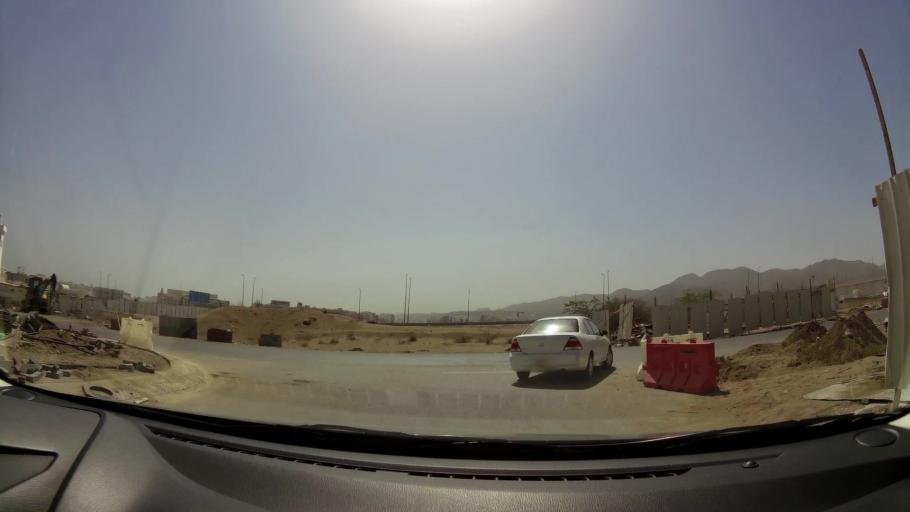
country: OM
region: Muhafazat Masqat
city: Bawshar
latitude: 23.5835
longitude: 58.4146
